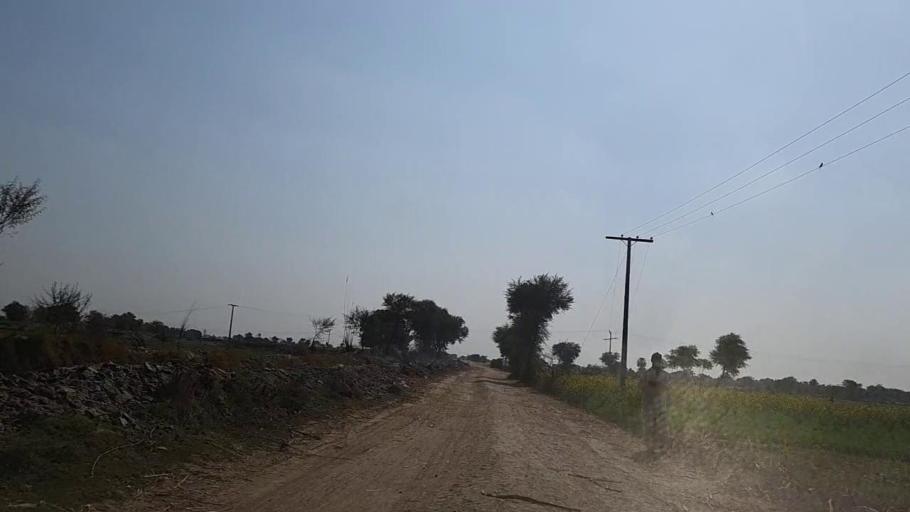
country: PK
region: Sindh
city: Daur
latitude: 26.4793
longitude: 68.2498
